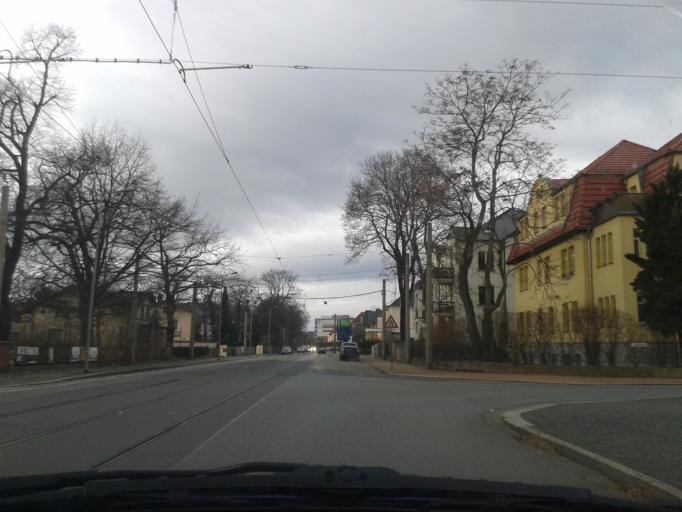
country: DE
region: Saxony
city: Radebeul
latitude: 51.0995
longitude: 13.6882
